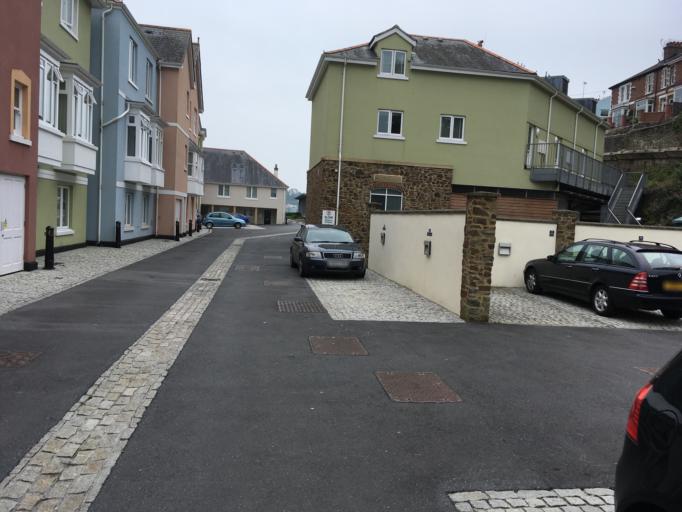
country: GB
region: England
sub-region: Devon
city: Dartmouth
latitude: 50.3584
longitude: -3.5779
